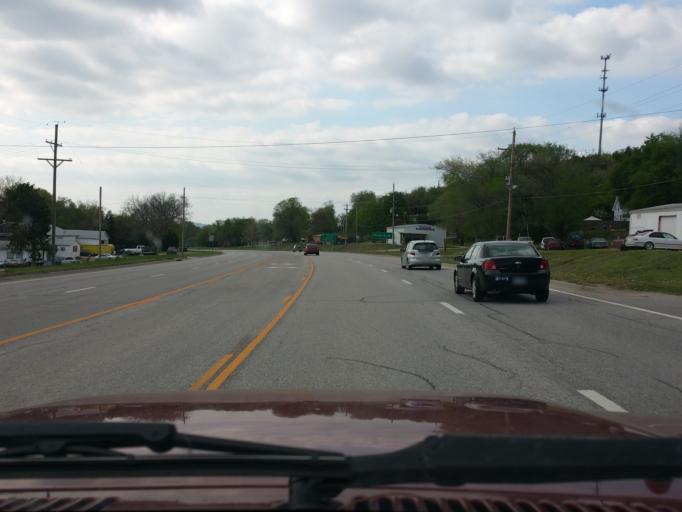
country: US
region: Kansas
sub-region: Riley County
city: Manhattan
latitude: 39.1692
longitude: -96.5418
